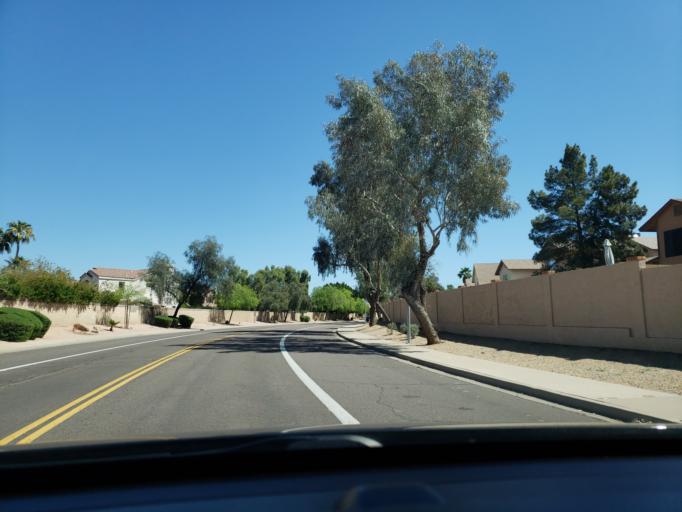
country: US
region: Arizona
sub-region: Maricopa County
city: Gilbert
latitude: 33.3835
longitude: -111.7498
